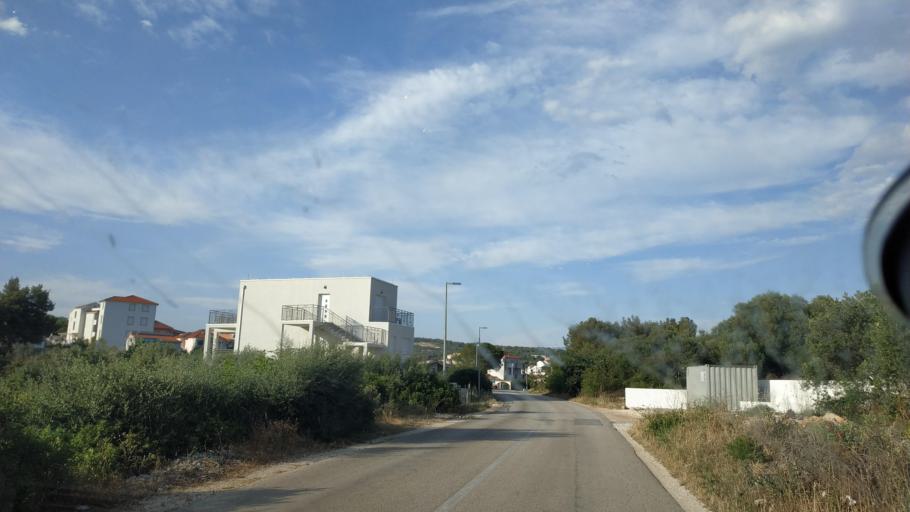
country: HR
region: Splitsko-Dalmatinska
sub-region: Grad Trogir
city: Trogir
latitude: 43.4890
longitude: 16.2520
